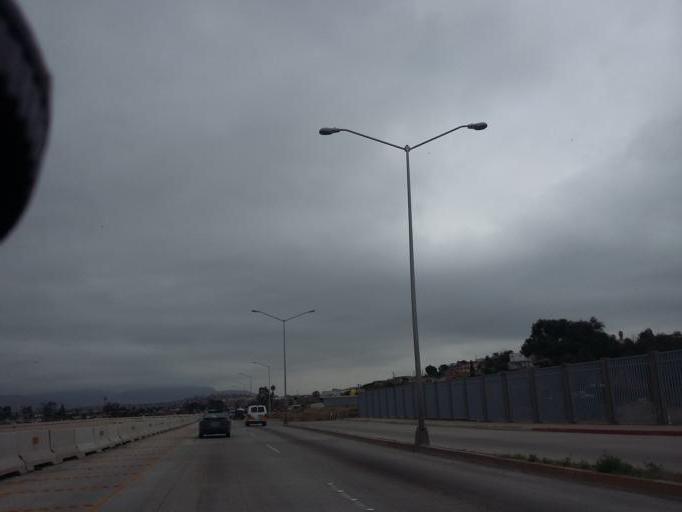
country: MX
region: Baja California
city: Tijuana
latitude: 32.5142
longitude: -116.9580
